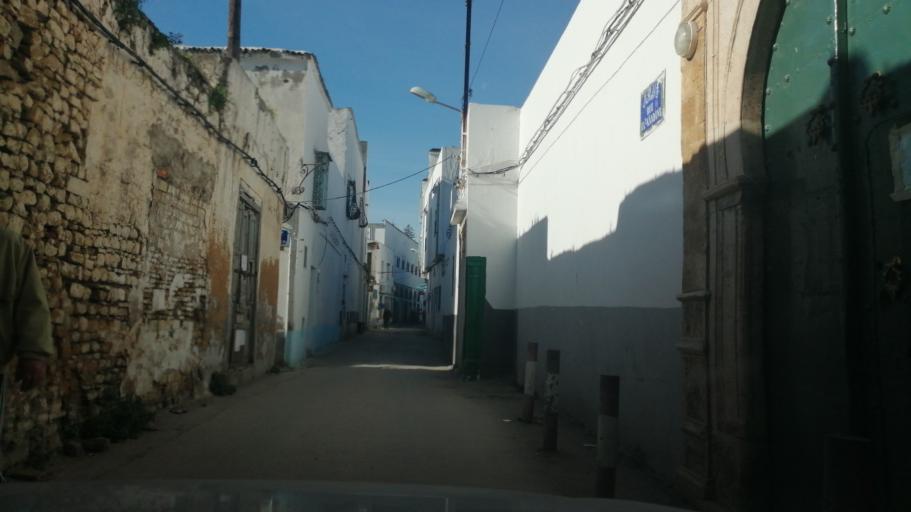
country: TN
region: Tunis
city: Tunis
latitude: 36.8044
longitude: 10.1665
